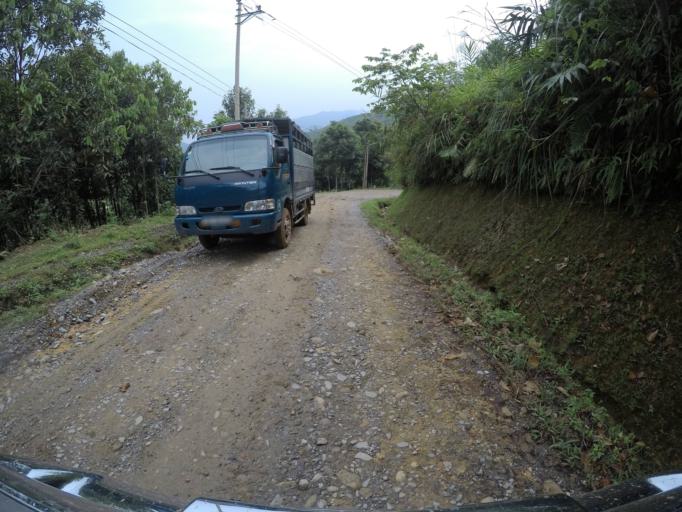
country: VN
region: Yen Bai
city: Co Phuc
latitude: 21.8130
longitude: 104.6273
